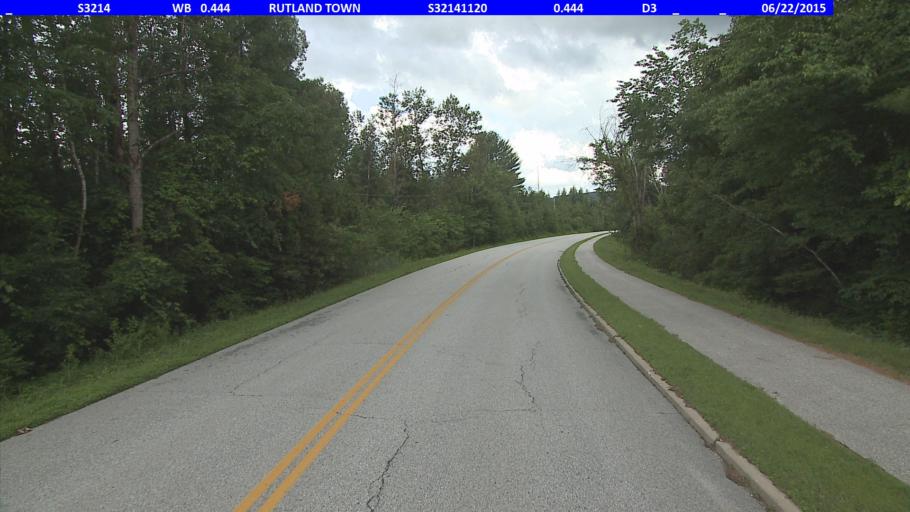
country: US
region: Vermont
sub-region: Rutland County
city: Rutland
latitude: 43.6354
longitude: -72.9675
